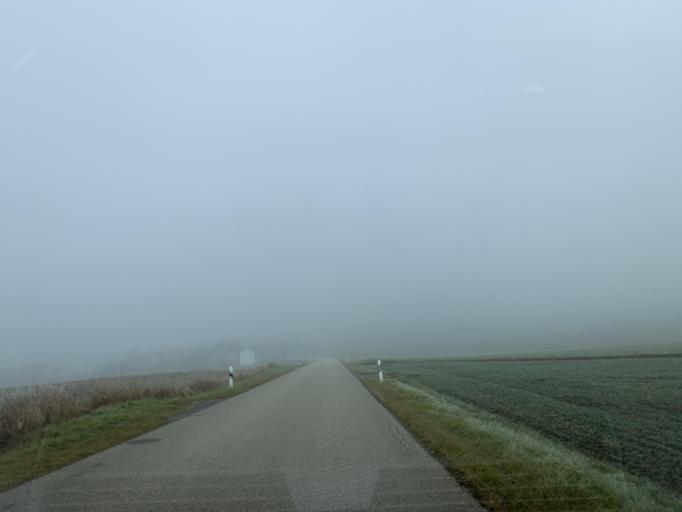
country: DE
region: Bavaria
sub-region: Upper Palatinate
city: Neunburg vorm Wald
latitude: 49.3672
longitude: 12.3889
